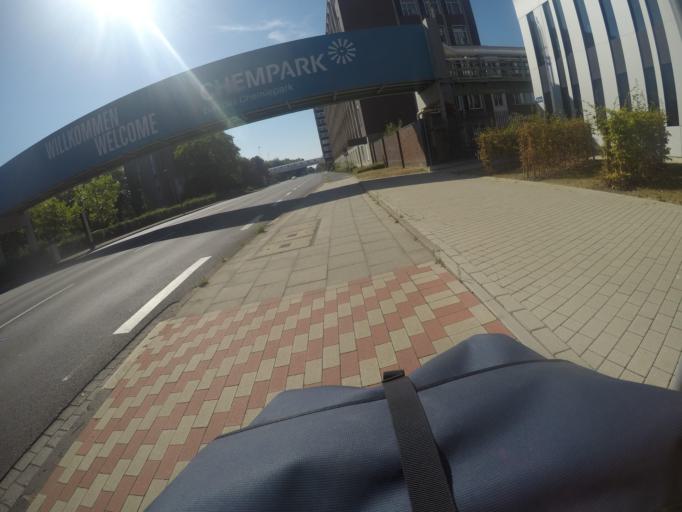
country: DE
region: North Rhine-Westphalia
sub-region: Regierungsbezirk Koln
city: Leverkusen
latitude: 51.0163
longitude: 6.9914
